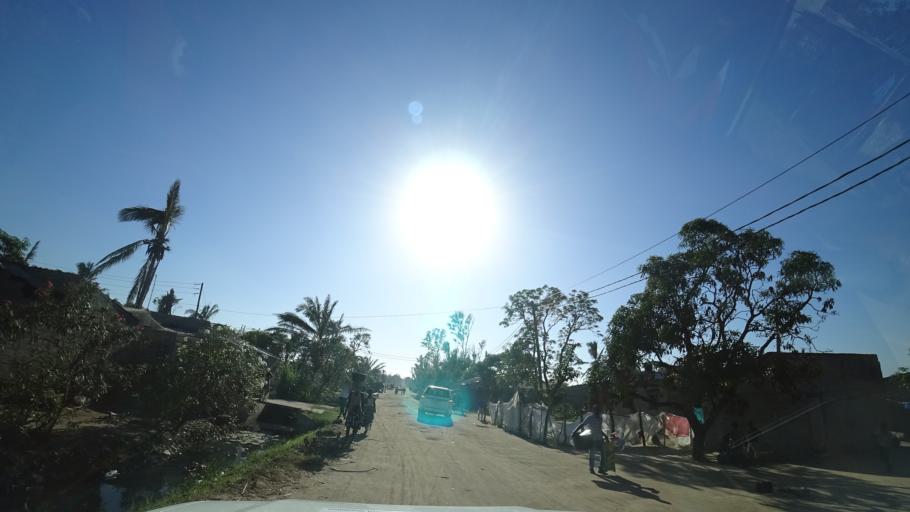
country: MZ
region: Sofala
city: Beira
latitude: -19.7703
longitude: 34.8886
